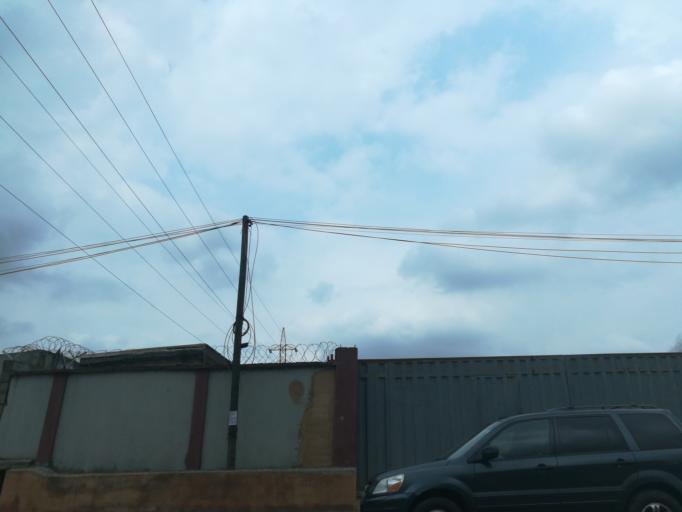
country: NG
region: Lagos
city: Agege
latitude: 6.6214
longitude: 3.3458
